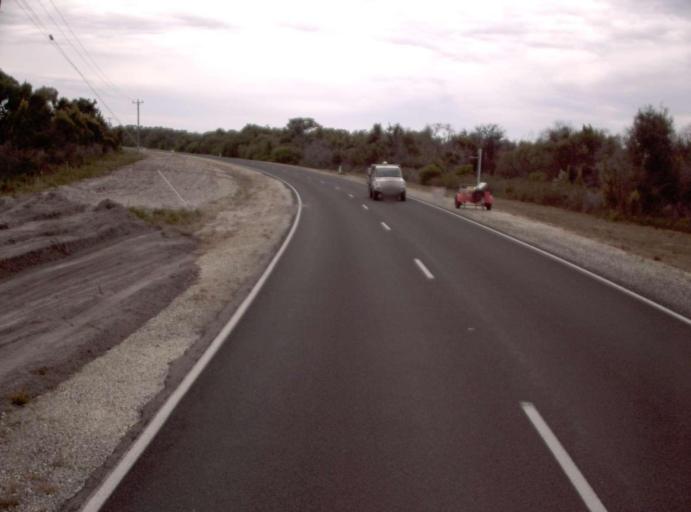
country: AU
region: Victoria
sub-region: East Gippsland
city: Bairnsdale
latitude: -38.1020
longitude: 147.5012
